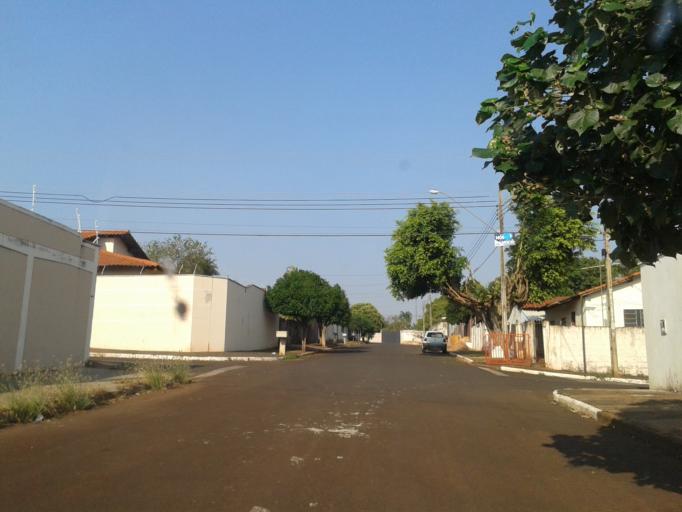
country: BR
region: Minas Gerais
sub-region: Ituiutaba
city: Ituiutaba
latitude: -18.9690
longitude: -49.4738
